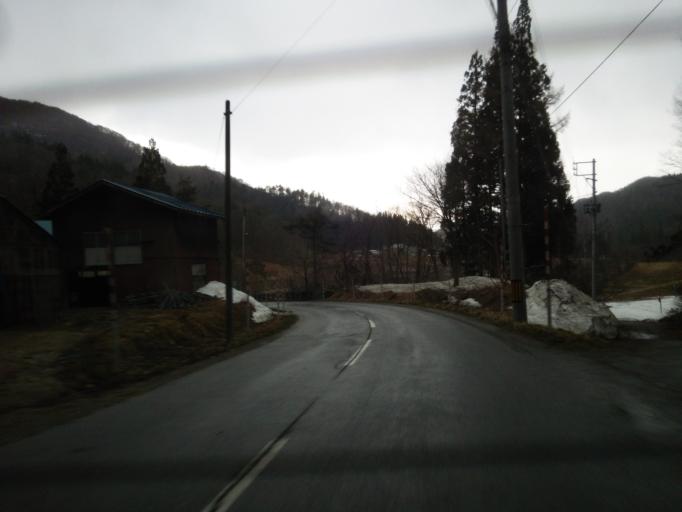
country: JP
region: Niigata
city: Muramatsu
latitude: 37.3144
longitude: 139.4520
